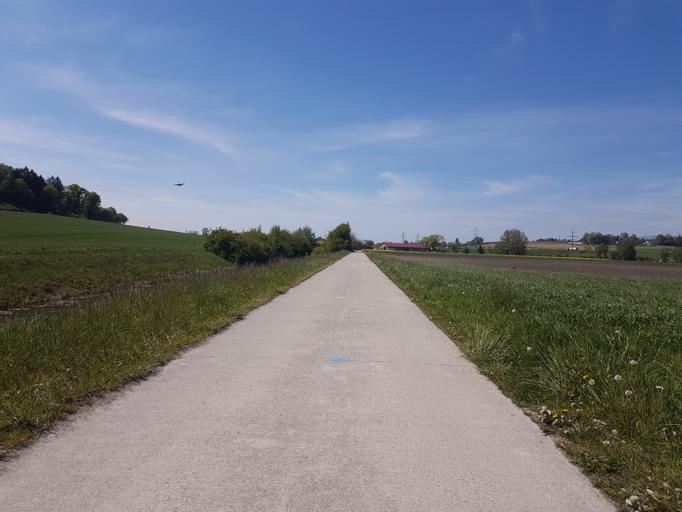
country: CH
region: Neuchatel
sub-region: Neuchatel District
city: Cornaux
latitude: 47.0319
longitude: 7.0394
